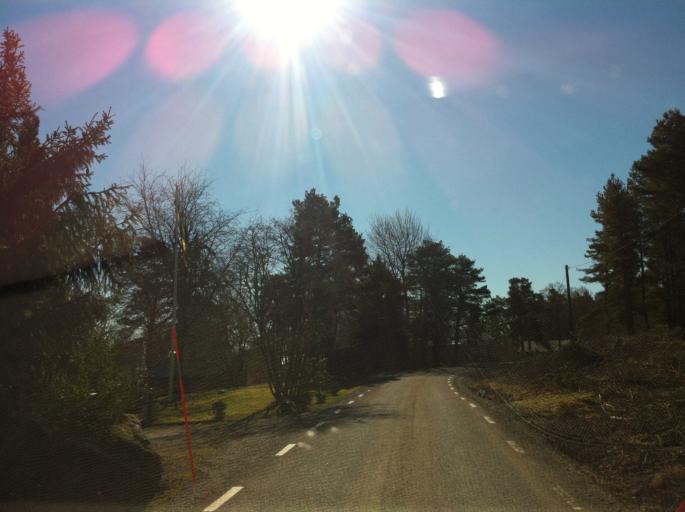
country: SE
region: Vaestra Goetaland
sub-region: Grastorps Kommun
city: Graestorp
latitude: 58.4572
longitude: 12.6213
